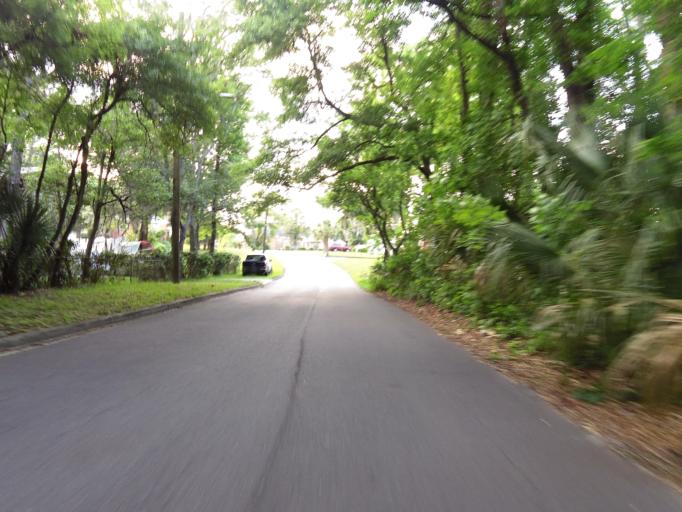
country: US
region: Florida
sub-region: Duval County
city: Jacksonville
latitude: 30.3047
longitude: -81.6265
